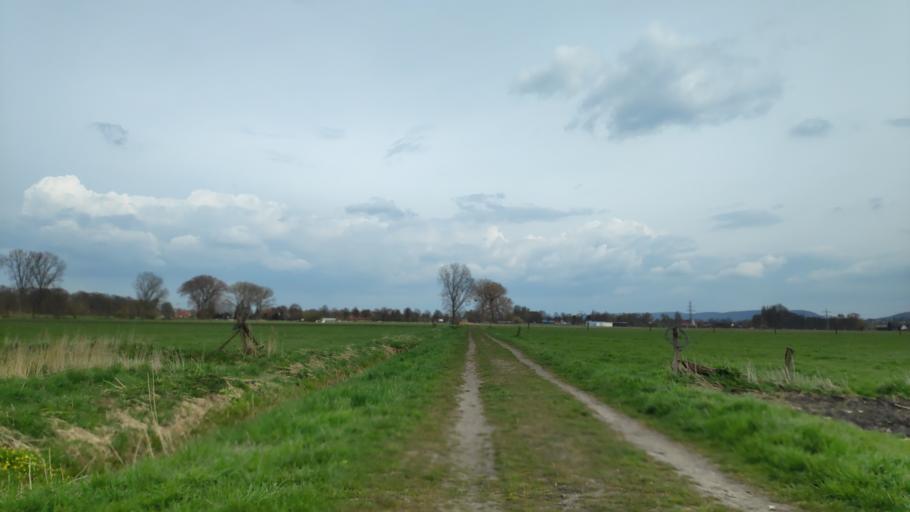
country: DE
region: North Rhine-Westphalia
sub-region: Regierungsbezirk Detmold
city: Minden
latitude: 52.2908
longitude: 8.8541
